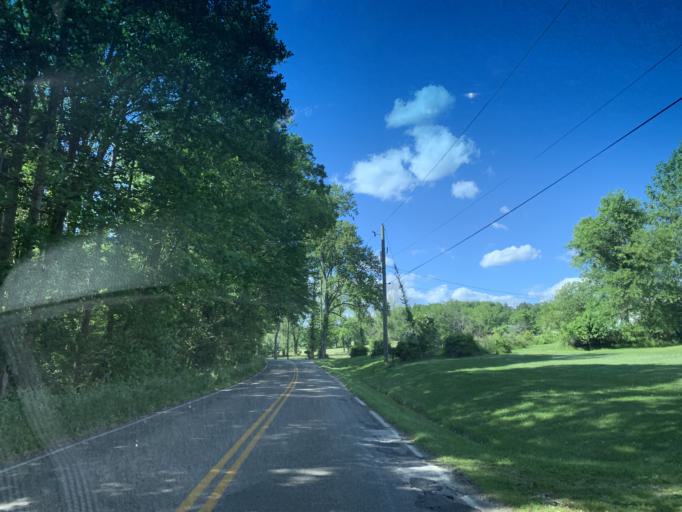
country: US
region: Maryland
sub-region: Cecil County
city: North East
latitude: 39.5438
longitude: -75.9179
